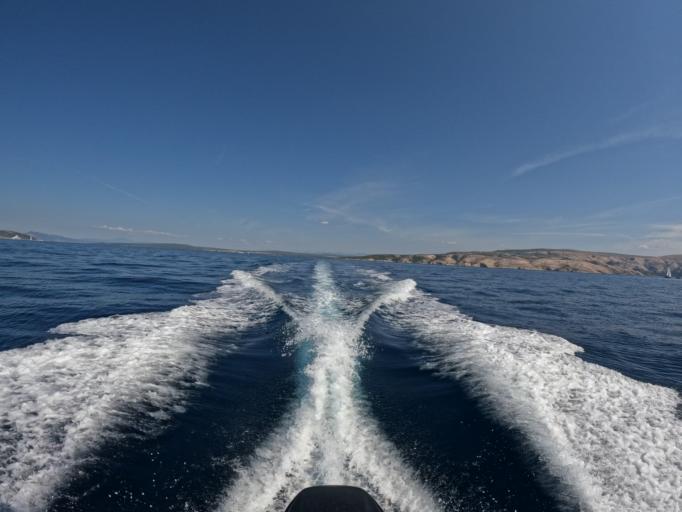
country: HR
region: Primorsko-Goranska
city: Punat
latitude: 44.9391
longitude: 14.6159
